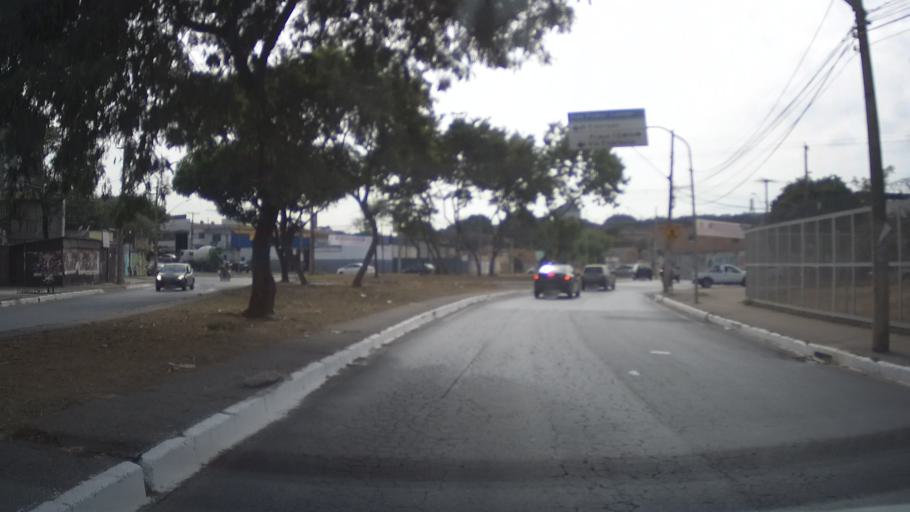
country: BR
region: Minas Gerais
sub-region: Contagem
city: Contagem
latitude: -19.9496
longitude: -44.0323
